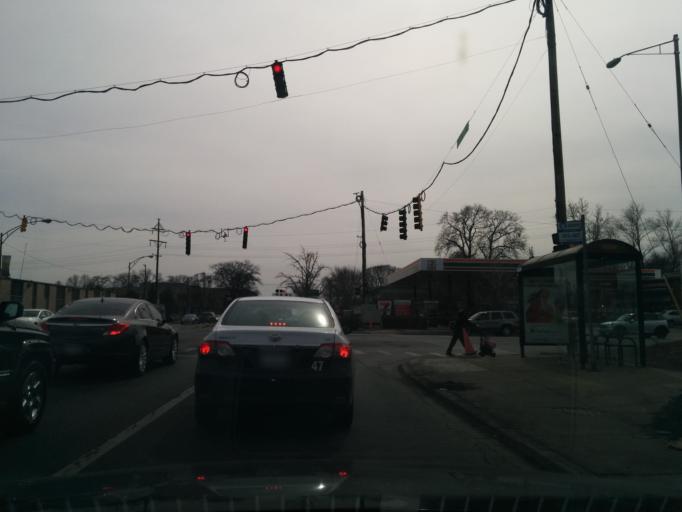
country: US
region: Illinois
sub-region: Cook County
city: Berwyn
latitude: 41.8434
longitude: -87.8035
